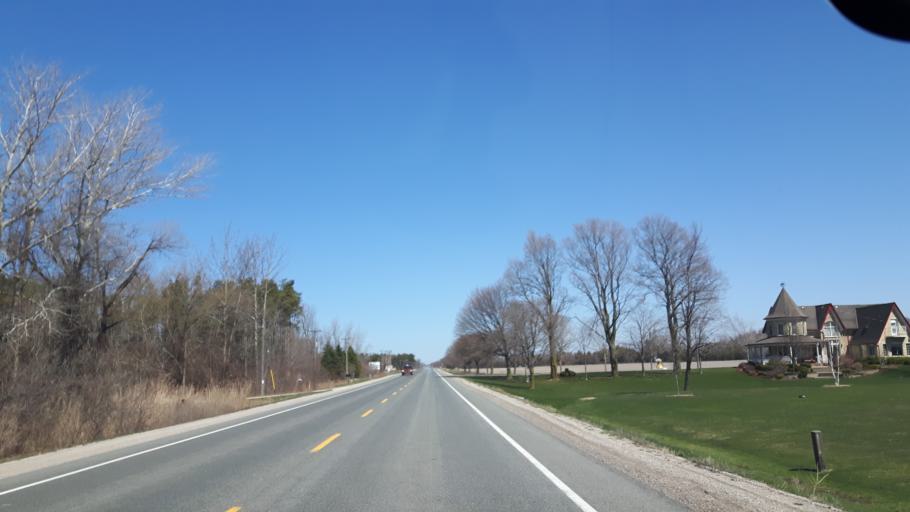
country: CA
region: Ontario
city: Goderich
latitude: 43.6996
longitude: -81.7056
